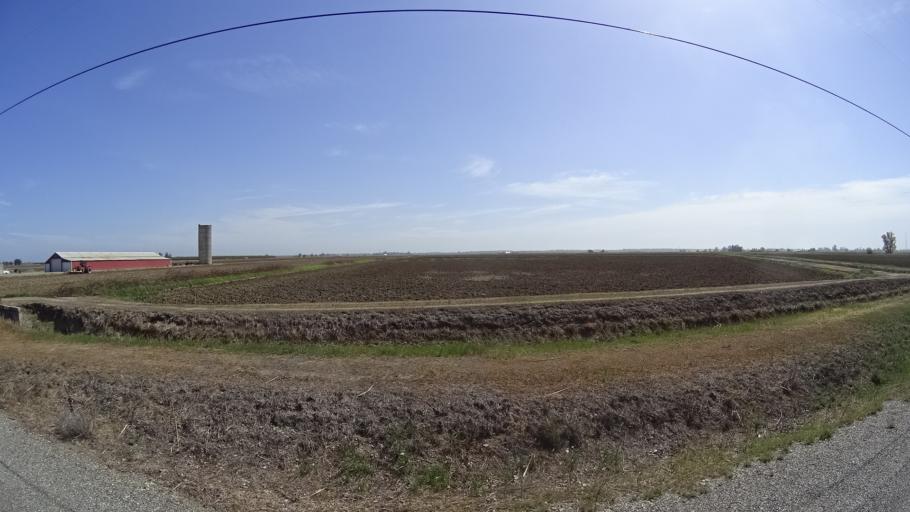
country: US
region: California
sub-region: Glenn County
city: Hamilton City
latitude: 39.6049
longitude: -122.0557
